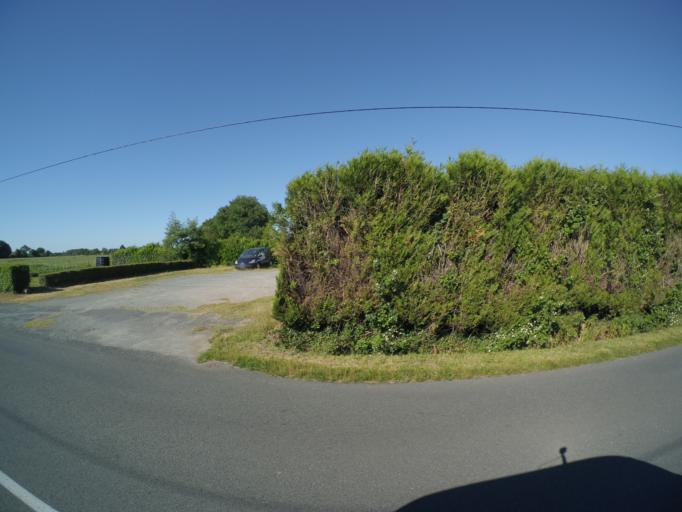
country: FR
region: Pays de la Loire
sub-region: Departement de la Vendee
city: La Boissiere-de-Montaigu
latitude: 46.9397
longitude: -1.1804
